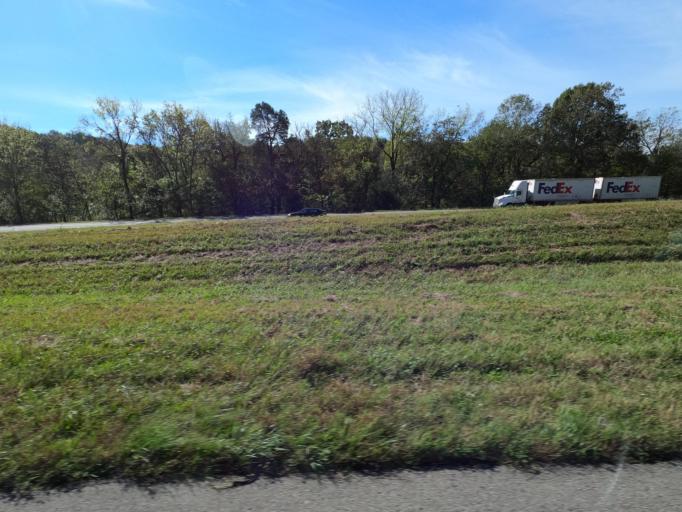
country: US
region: Tennessee
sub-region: Dickson County
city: Burns
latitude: 36.0177
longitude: -87.2498
